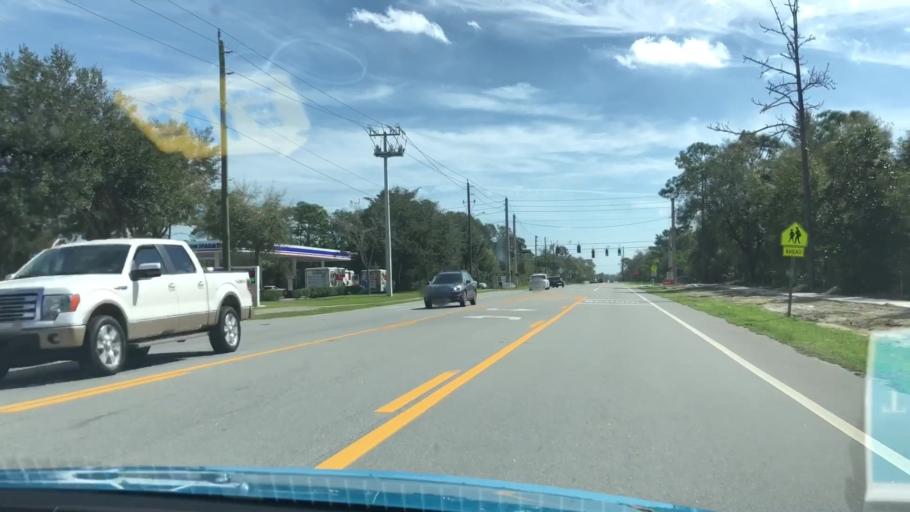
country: US
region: Florida
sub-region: Seminole County
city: Midway
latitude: 28.8568
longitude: -81.1876
